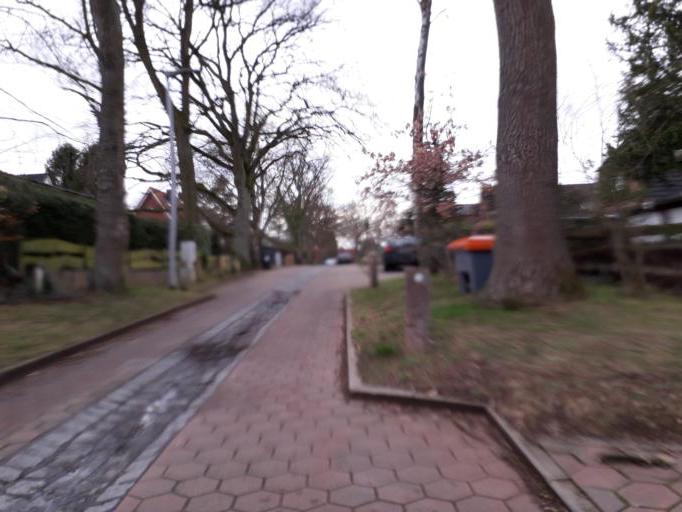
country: DE
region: Schleswig-Holstein
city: Glinde
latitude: 53.5548
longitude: 10.2106
